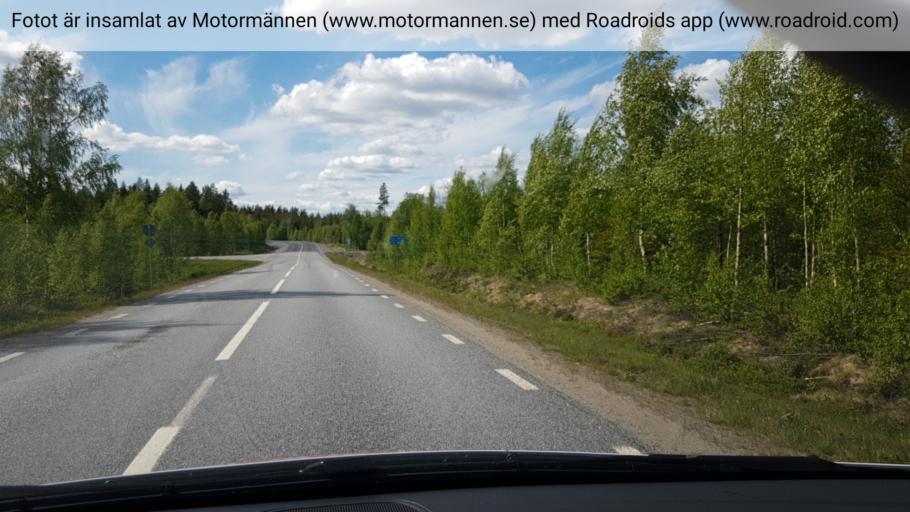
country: SE
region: Vaesterbotten
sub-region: Skelleftea Kommun
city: Burtraesk
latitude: 64.5110
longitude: 20.4619
